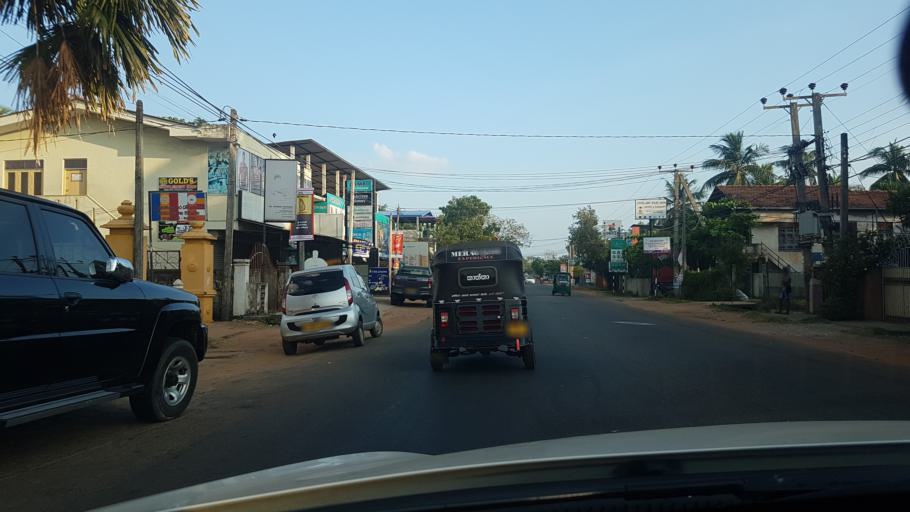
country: LK
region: North Western
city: Chilaw
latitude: 7.5685
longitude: 79.7994
